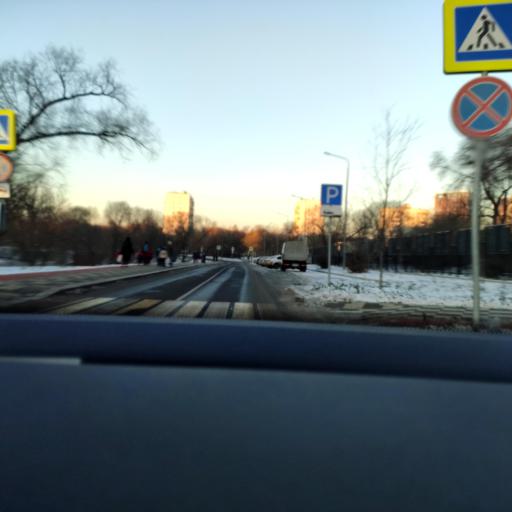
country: RU
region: Moskovskaya
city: Bogorodskoye
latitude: 55.8058
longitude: 37.7332
